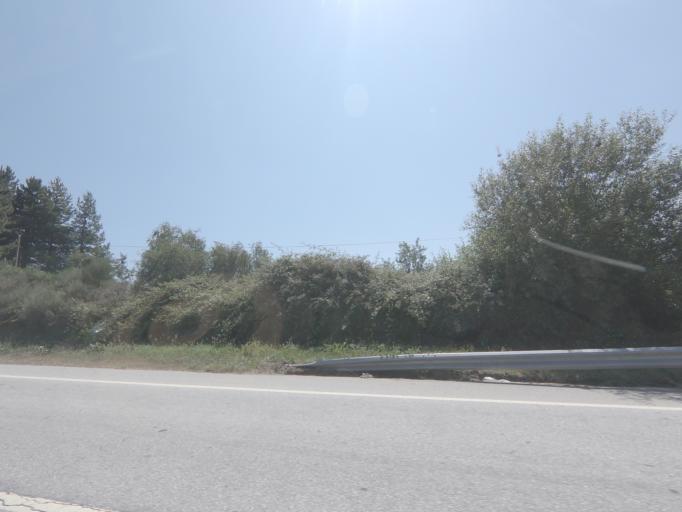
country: PT
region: Viseu
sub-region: Castro Daire
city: Castro Daire
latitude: 40.9744
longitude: -7.8857
